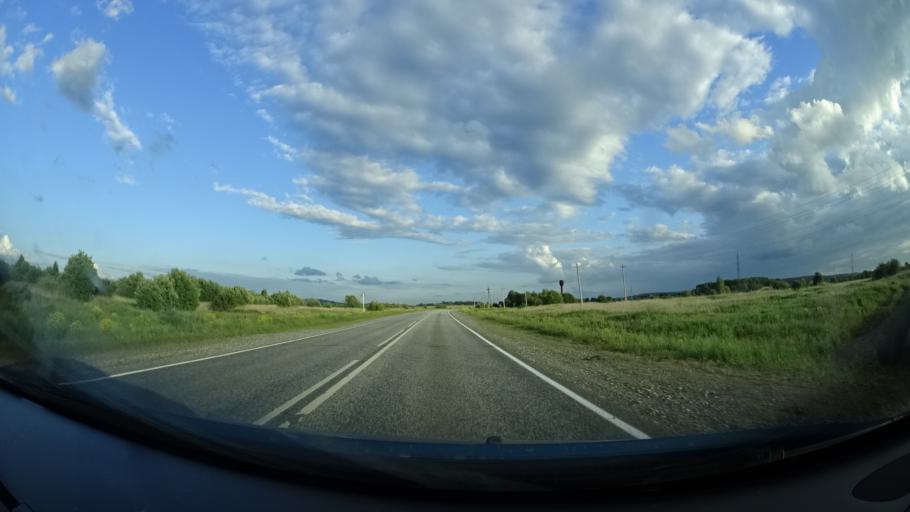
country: RU
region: Perm
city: Barda
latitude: 57.0847
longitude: 55.5413
